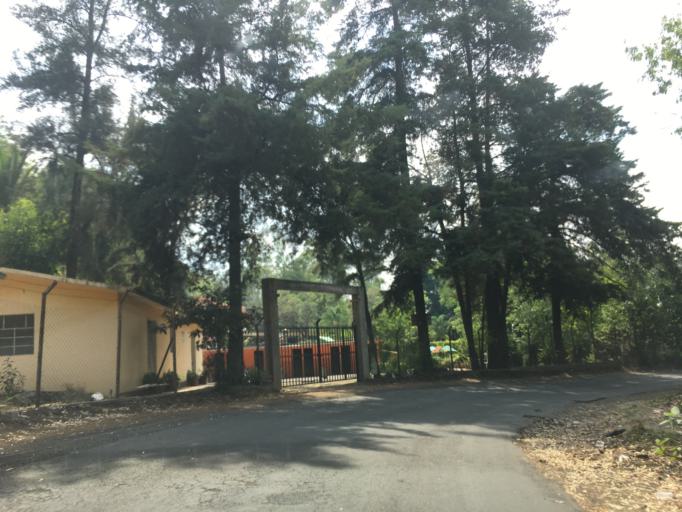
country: MX
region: Michoacan
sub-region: Morelia
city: La Mintzita (Piedra Dura)
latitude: 19.6396
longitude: -101.2733
